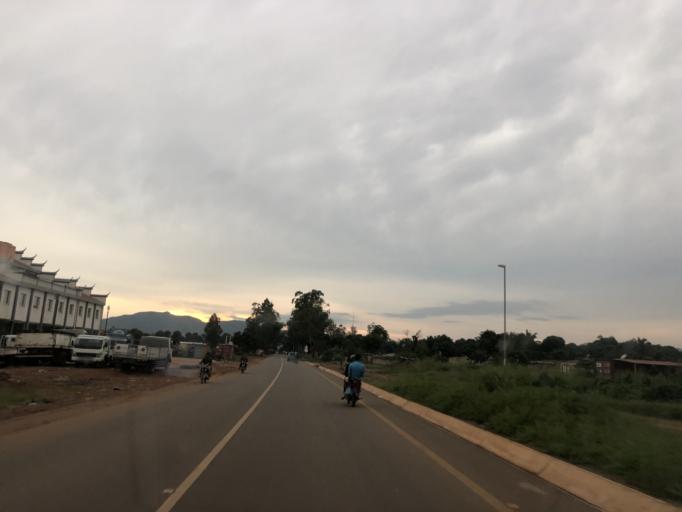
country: AO
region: Cuanza Sul
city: Uacu Cungo
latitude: -11.3518
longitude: 15.1141
